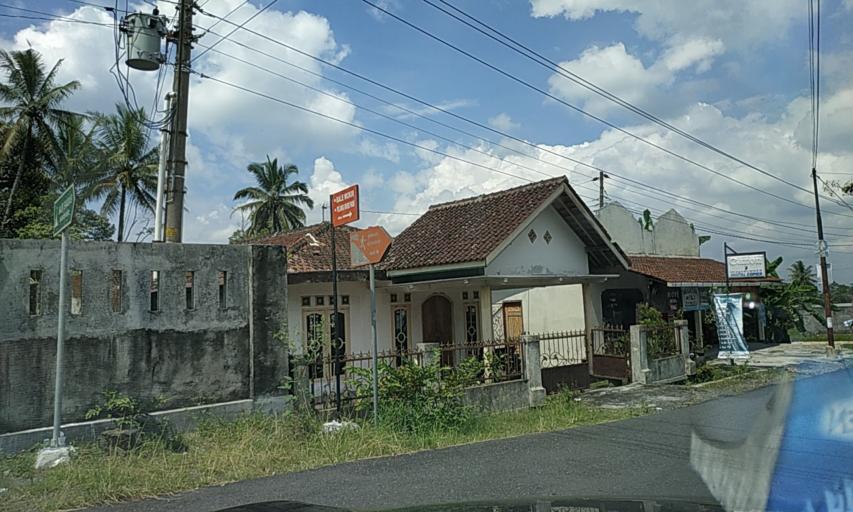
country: ID
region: Central Java
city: Jogonalan
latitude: -7.6582
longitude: 110.4442
